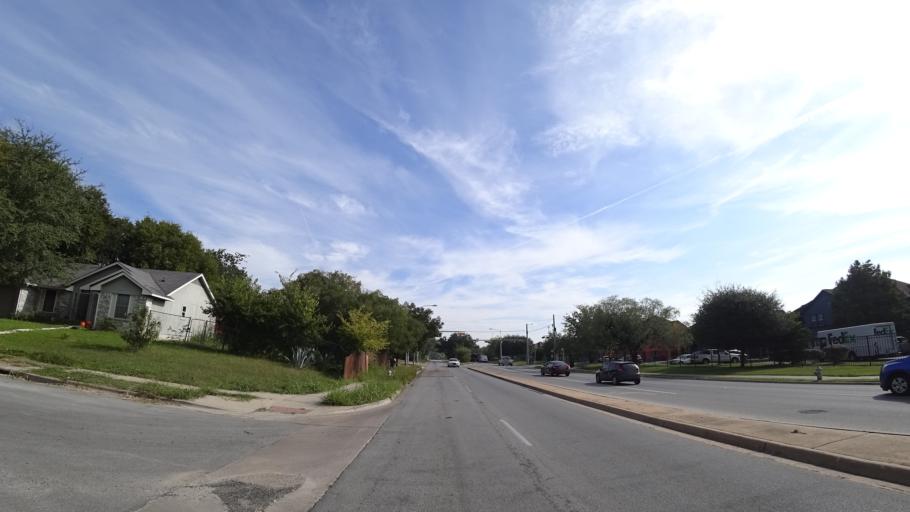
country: US
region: Texas
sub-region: Travis County
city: Onion Creek
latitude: 30.1911
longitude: -97.7317
